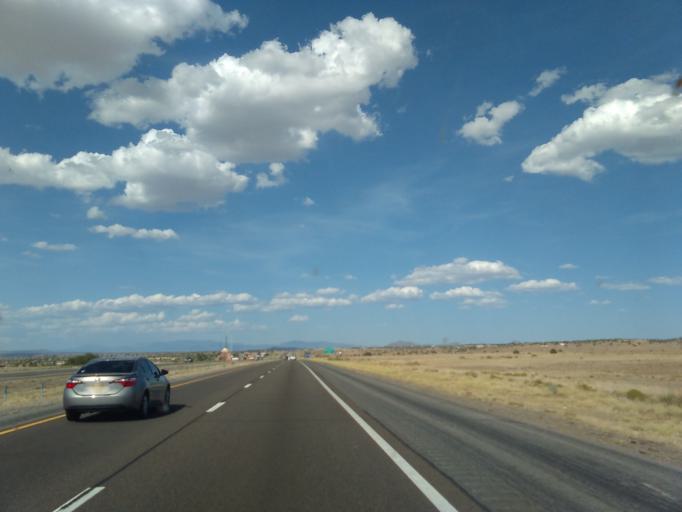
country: US
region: New Mexico
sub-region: Sandoval County
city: Santo Domingo Pueblo
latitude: 35.4497
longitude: -106.3541
